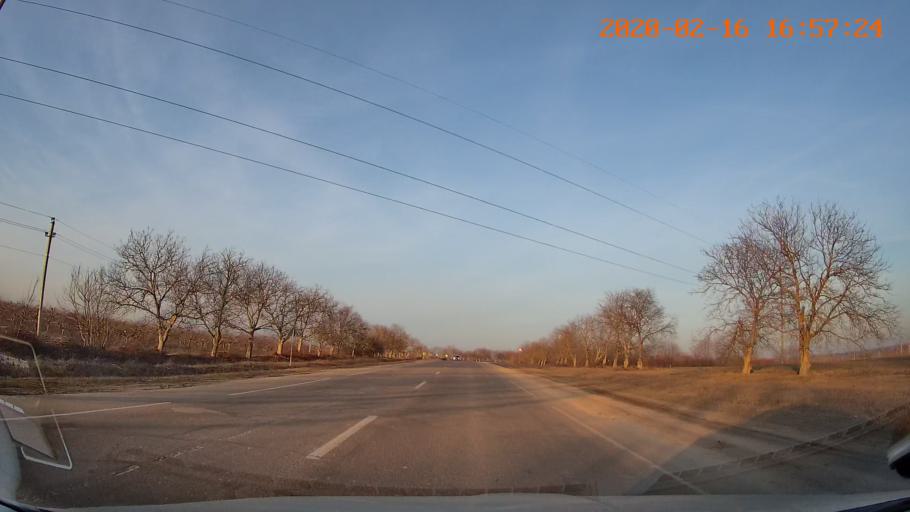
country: MD
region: Briceni
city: Briceni
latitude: 48.3417
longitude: 27.0679
